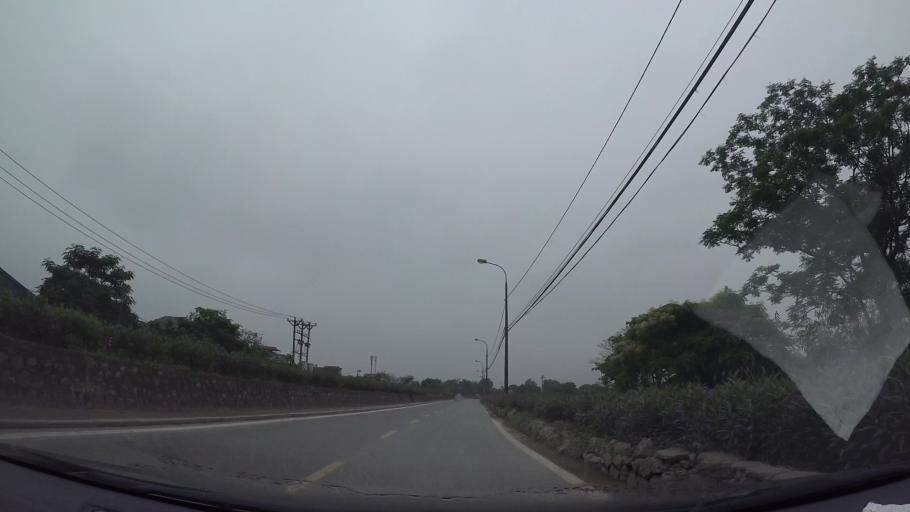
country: VN
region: Hung Yen
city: Van Giang
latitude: 20.9812
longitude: 105.8942
